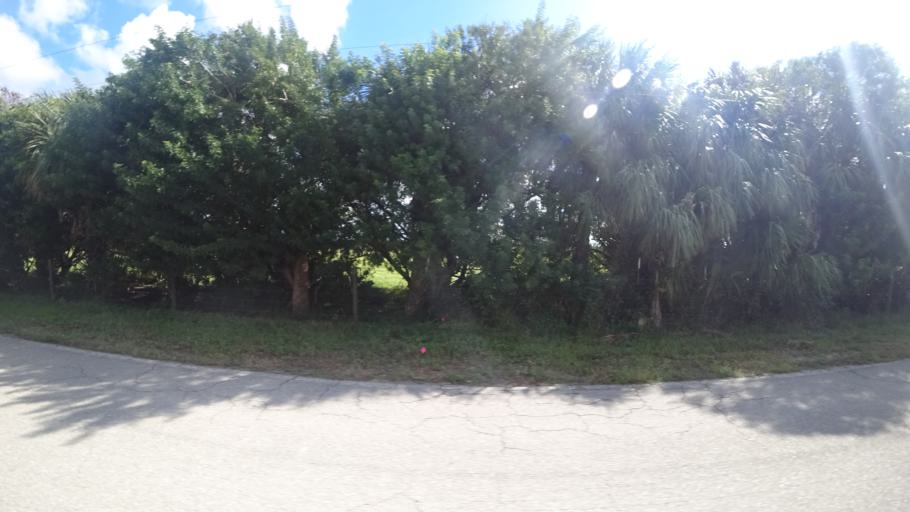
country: US
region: Florida
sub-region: Manatee County
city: Ellenton
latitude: 27.6087
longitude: -82.4817
